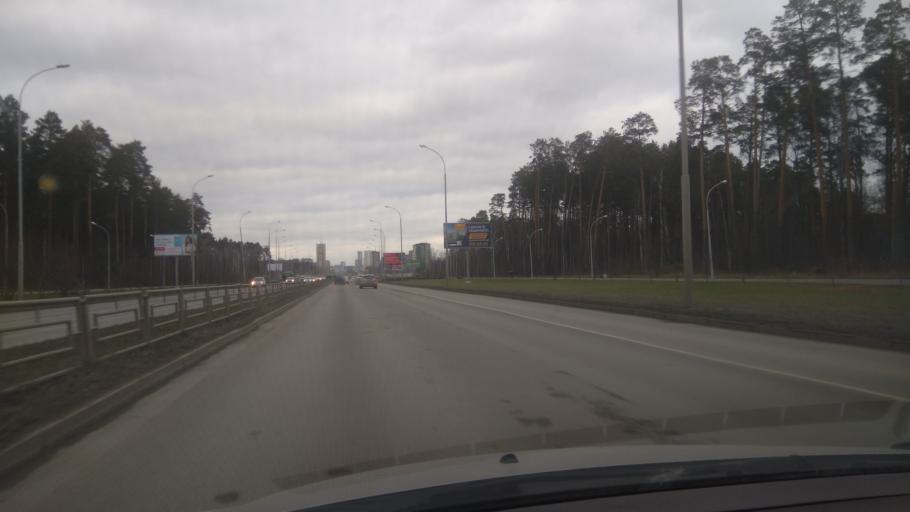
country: RU
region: Sverdlovsk
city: Sovkhoznyy
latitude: 56.7998
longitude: 60.5338
